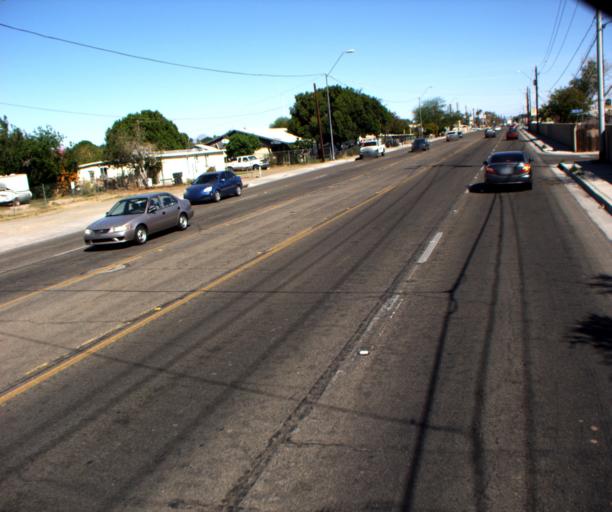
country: US
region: Arizona
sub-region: Yuma County
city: Yuma
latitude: 32.6948
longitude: -114.6504
